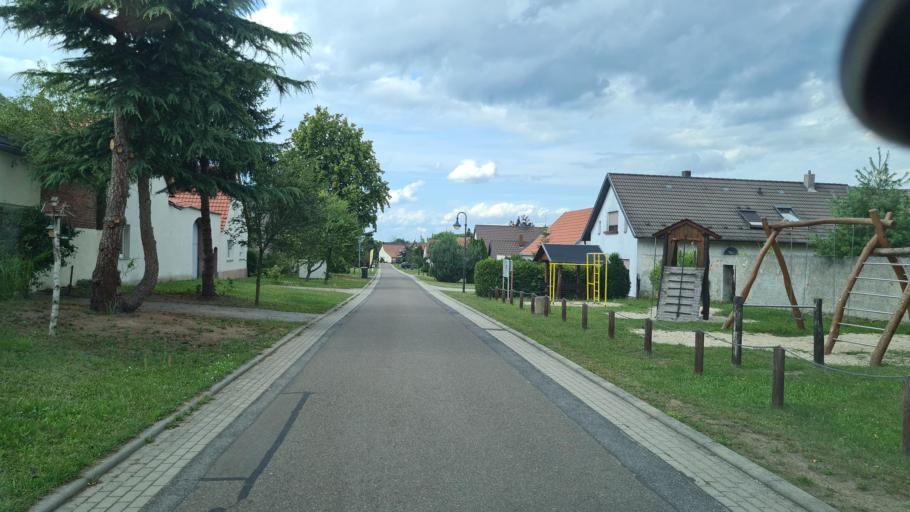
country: DE
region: Brandenburg
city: Drebkau
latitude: 51.6357
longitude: 14.1915
